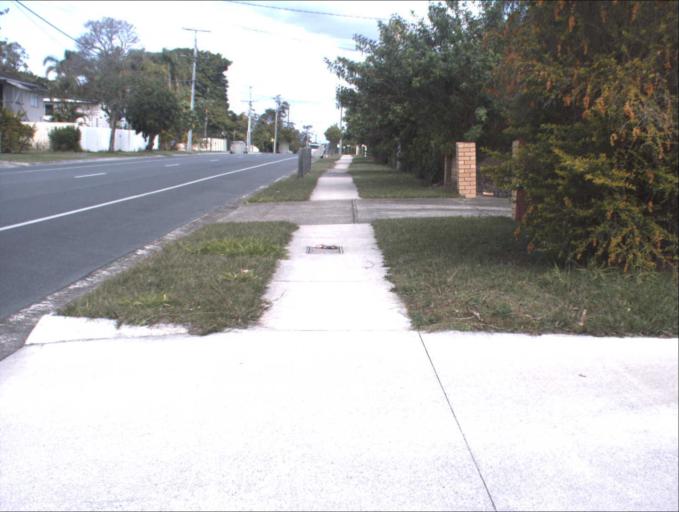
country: AU
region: Queensland
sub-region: Logan
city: Logan City
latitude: -27.6716
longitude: 153.0860
